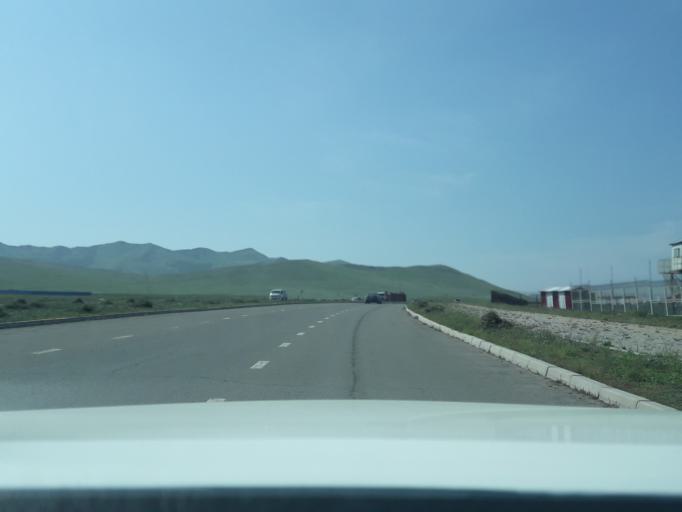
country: MN
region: Ulaanbaatar
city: Ulaanbaatar
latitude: 47.8305
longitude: 106.7859
